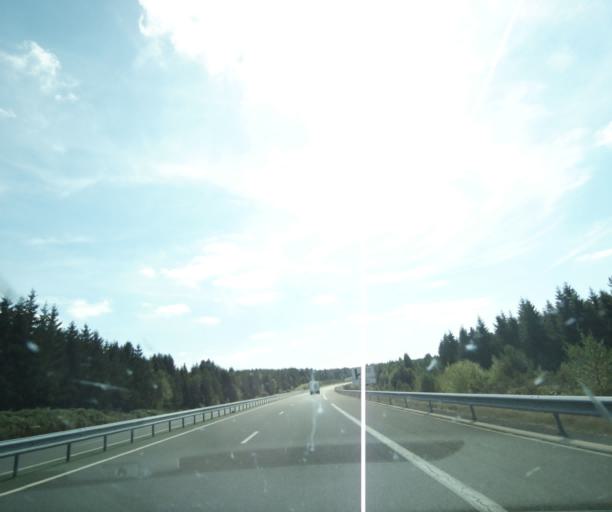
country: FR
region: Auvergne
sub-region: Departement du Puy-de-Dome
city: Saint-Sauves-d'Auvergne
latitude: 45.6894
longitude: 2.6961
